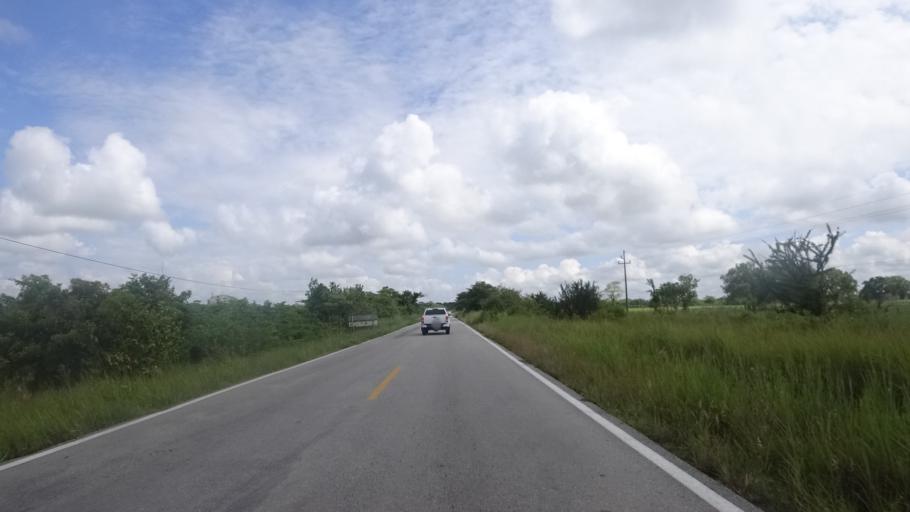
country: MX
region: Chiapas
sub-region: Catazaja
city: Catazaja
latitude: 17.6929
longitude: -92.0218
